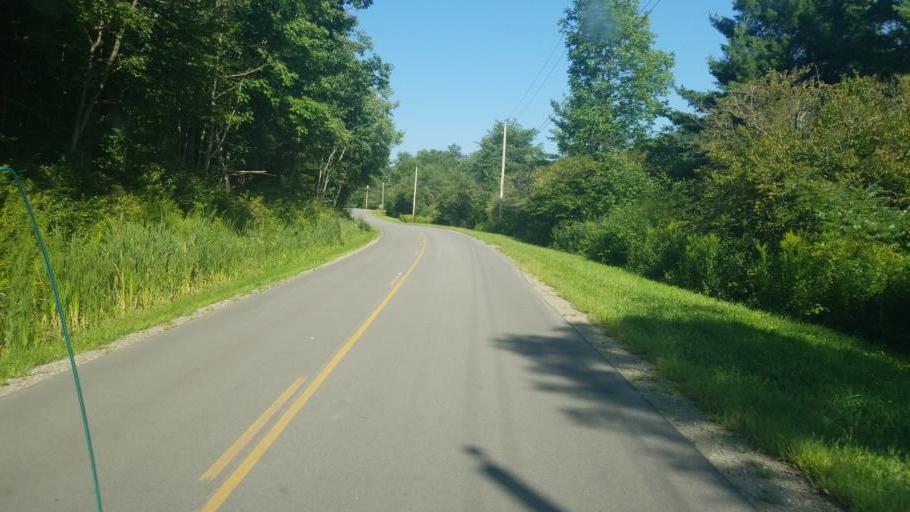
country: US
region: New York
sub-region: Allegany County
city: Wellsville
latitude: 42.0138
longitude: -78.0100
